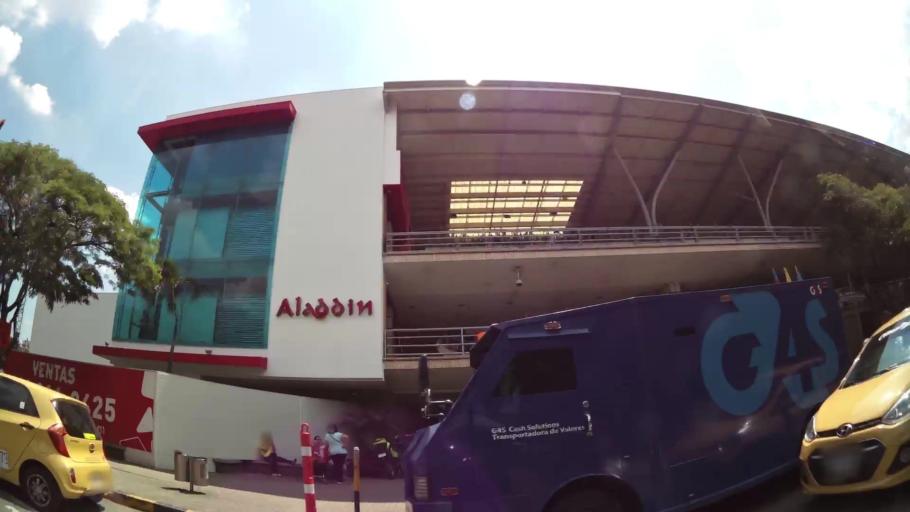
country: CO
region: Valle del Cauca
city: Cali
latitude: 3.4150
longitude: -76.5469
